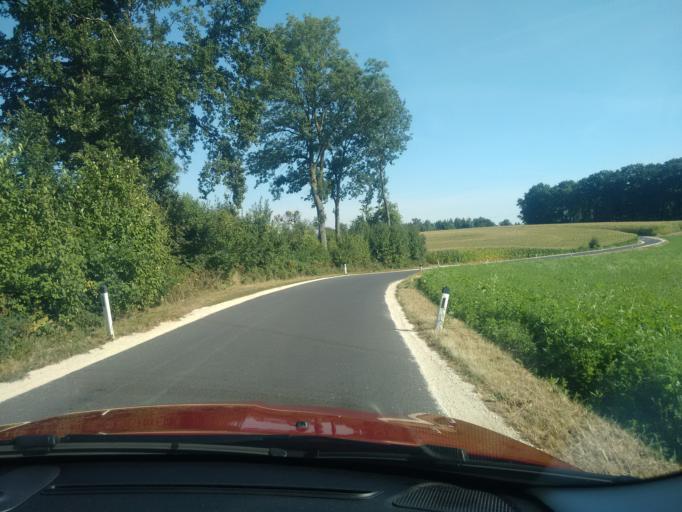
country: AT
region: Upper Austria
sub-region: Wels-Land
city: Sattledt
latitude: 48.0771
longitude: 14.0710
